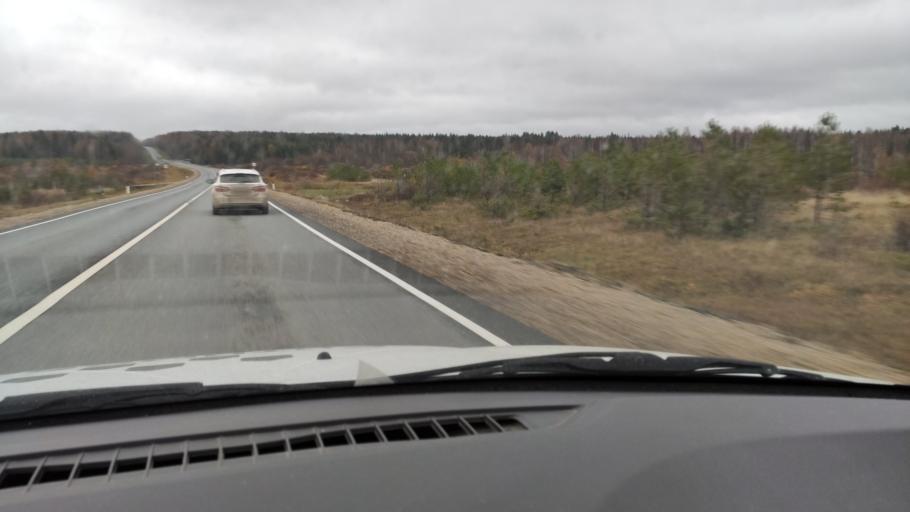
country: RU
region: Kirov
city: Chernaya Kholunitsa
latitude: 58.8589
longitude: 51.6997
